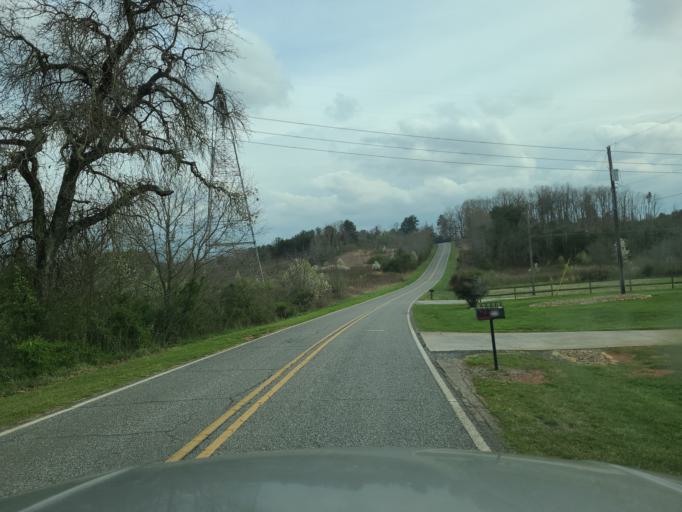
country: US
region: North Carolina
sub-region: Cleveland County
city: Boiling Springs
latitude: 35.2345
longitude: -81.7364
